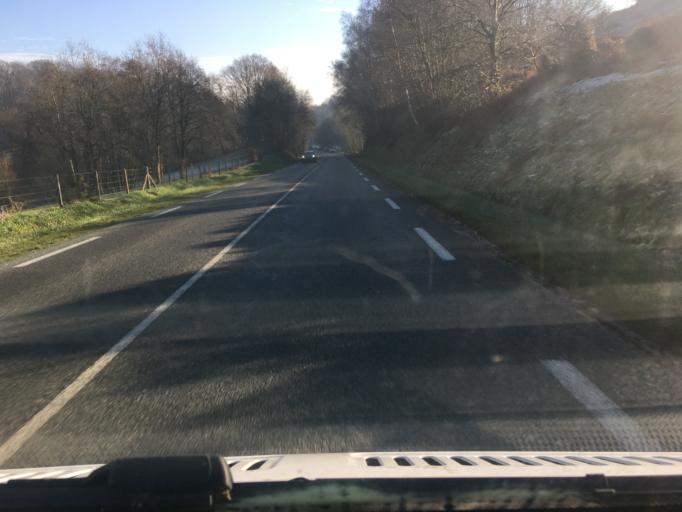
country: FR
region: Haute-Normandie
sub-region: Departement de la Seine-Maritime
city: Yvetot
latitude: 49.6054
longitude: 0.7502
